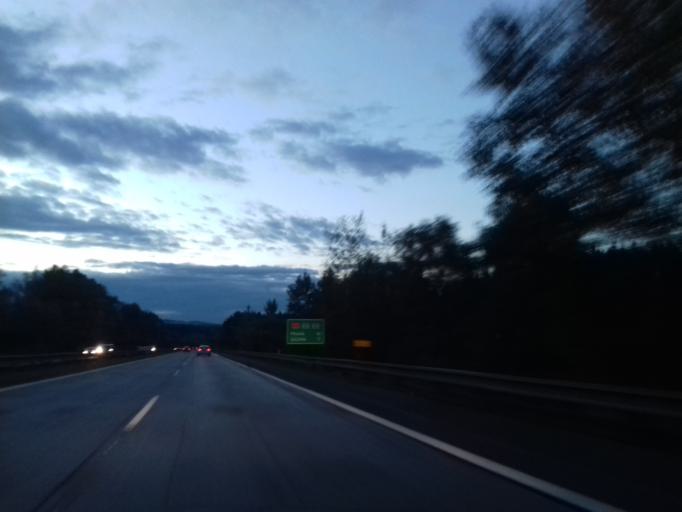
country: CZ
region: Central Bohemia
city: Divisov
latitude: 49.8051
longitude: 14.8987
